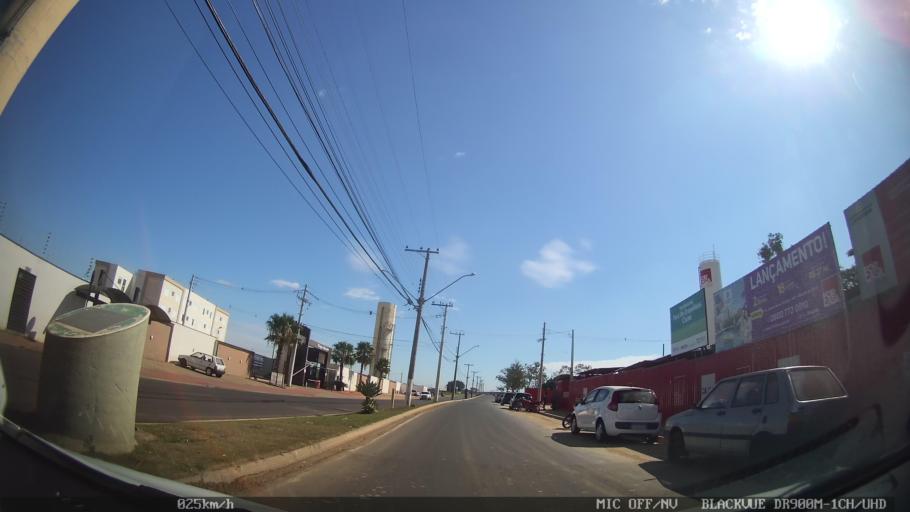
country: BR
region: Sao Paulo
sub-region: Santa Barbara D'Oeste
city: Santa Barbara d'Oeste
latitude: -22.7285
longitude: -47.3983
